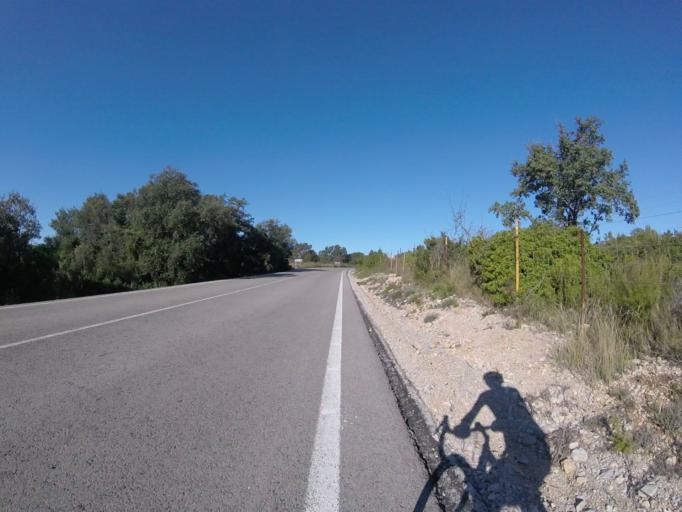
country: ES
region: Valencia
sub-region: Provincia de Castello
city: Cervera del Maestre
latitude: 40.4737
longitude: 0.2322
